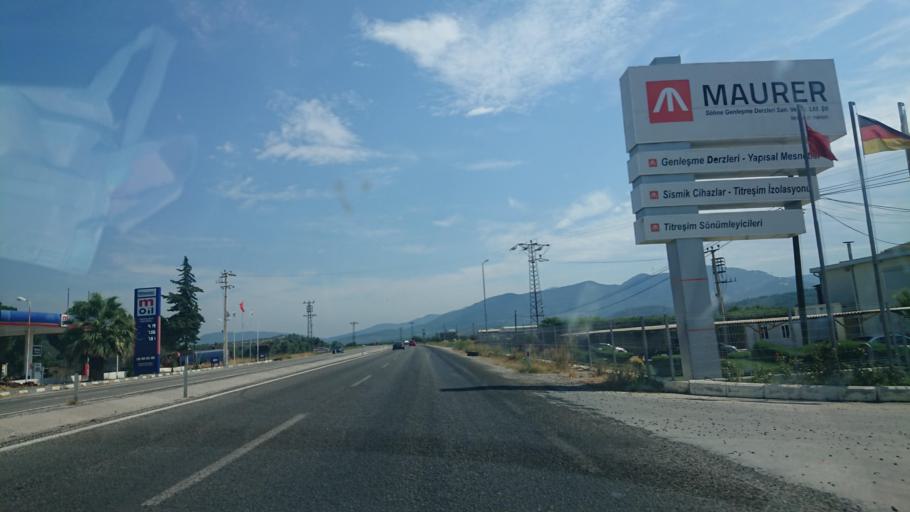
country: TR
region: Izmir
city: Dagkizilca
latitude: 38.2538
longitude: 27.3854
